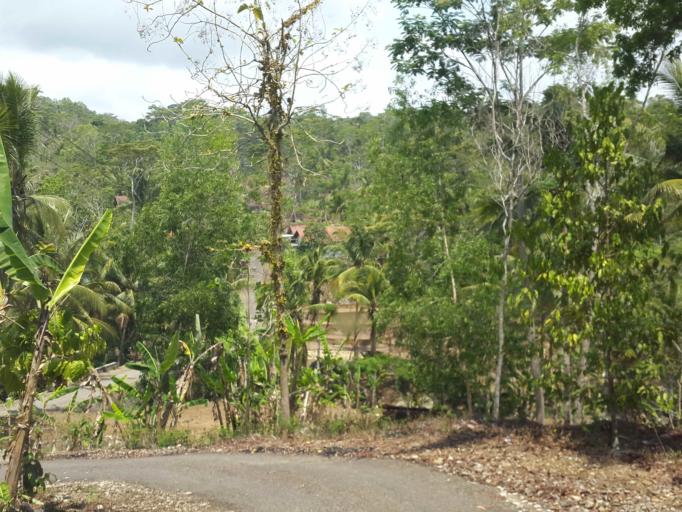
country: ID
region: East Java
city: Sudimoro
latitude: -8.2411
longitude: 111.2274
